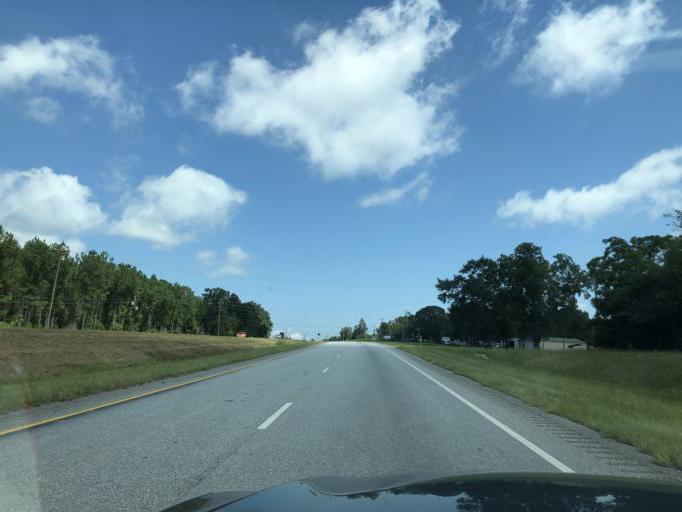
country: US
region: Alabama
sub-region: Barbour County
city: Eufaula
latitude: 31.7756
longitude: -85.1797
